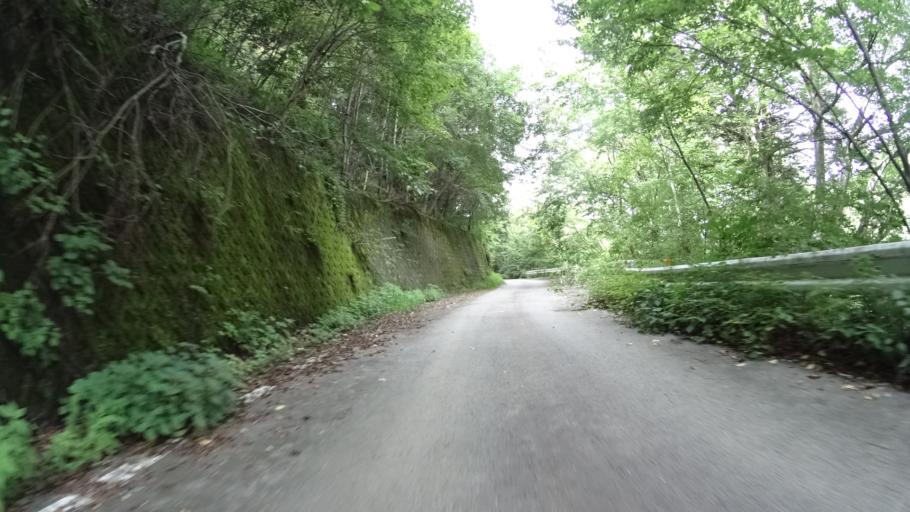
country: JP
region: Yamanashi
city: Nirasaki
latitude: 35.8055
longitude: 138.5329
